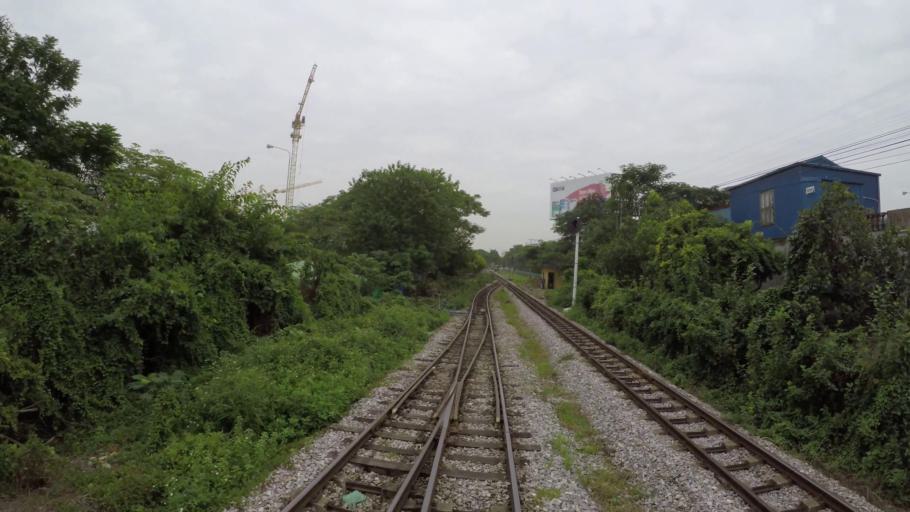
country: VN
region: Hai Phong
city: An Duong
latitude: 20.8777
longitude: 106.6301
